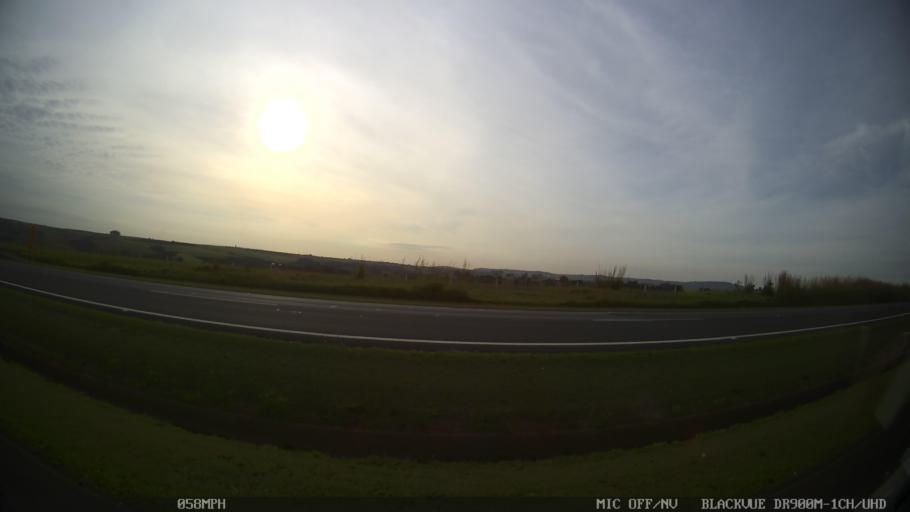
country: BR
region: Sao Paulo
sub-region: Iracemapolis
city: Iracemapolis
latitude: -22.6162
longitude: -47.4824
